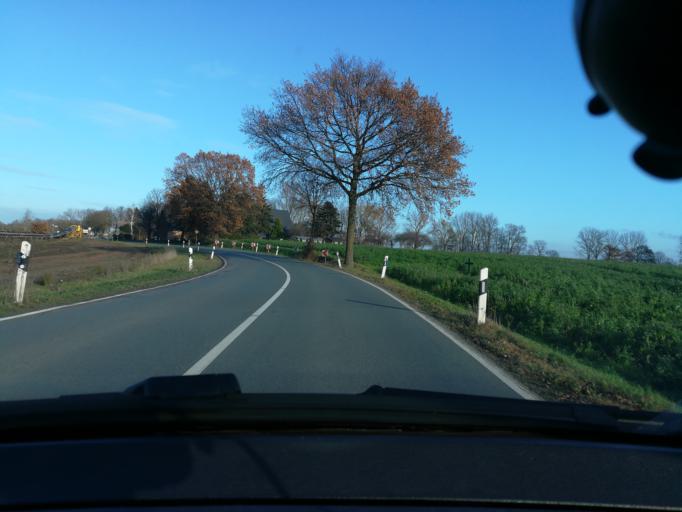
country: DE
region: North Rhine-Westphalia
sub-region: Regierungsbezirk Detmold
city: Minden
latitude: 52.3250
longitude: 8.9481
